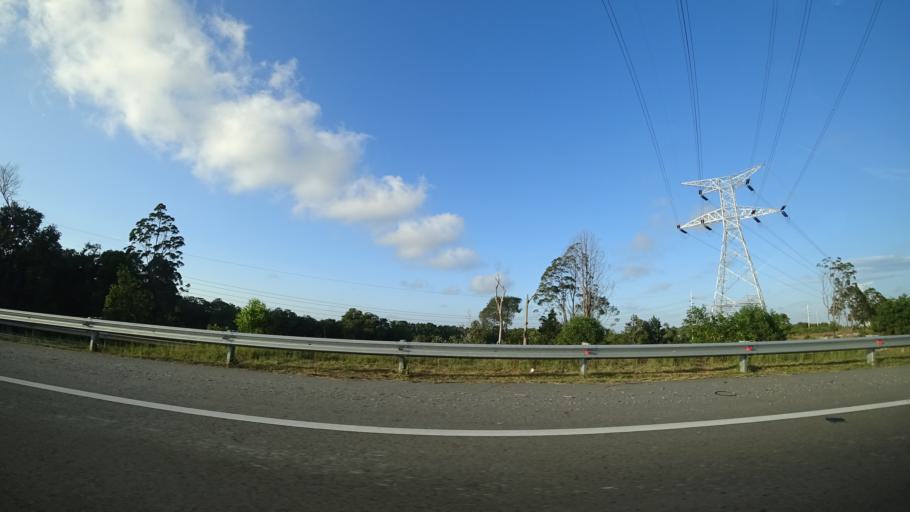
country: BN
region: Tutong
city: Tutong
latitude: 4.7343
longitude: 114.5786
